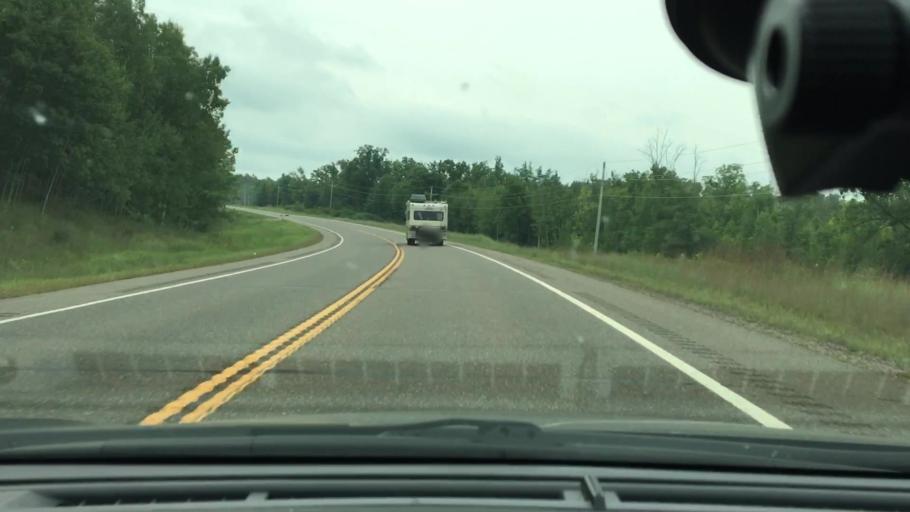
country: US
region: Minnesota
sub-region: Crow Wing County
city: Crosby
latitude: 46.5086
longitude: -93.9601
